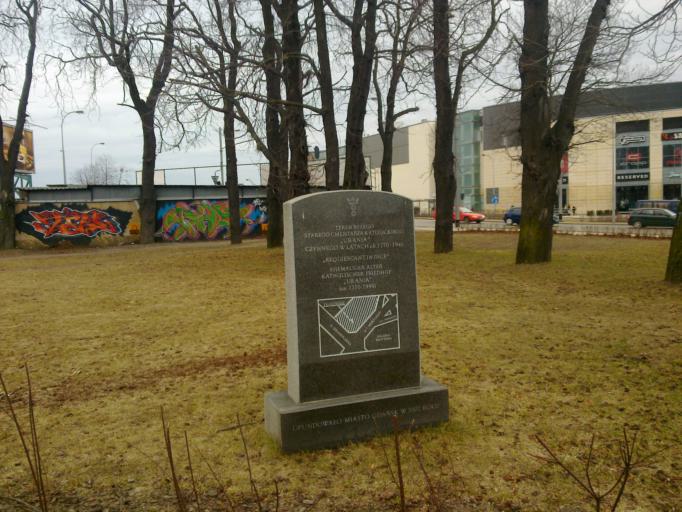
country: PL
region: Pomeranian Voivodeship
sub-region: Gdansk
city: Gdansk
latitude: 54.3833
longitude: 18.5979
